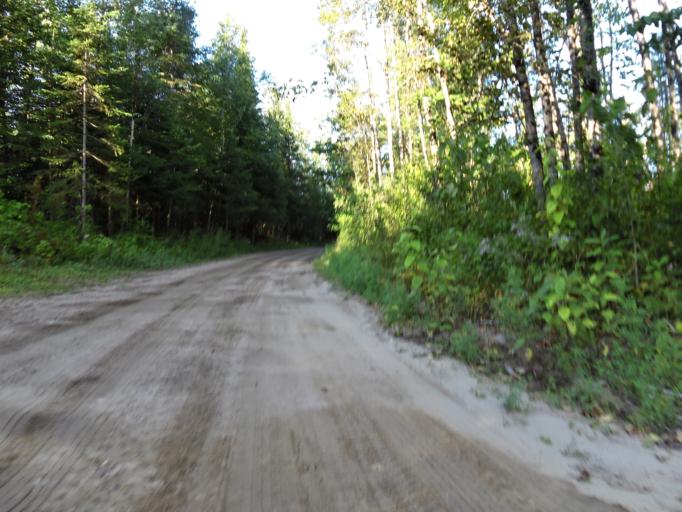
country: CA
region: Quebec
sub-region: Outaouais
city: Maniwaki
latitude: 46.3062
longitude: -76.0109
